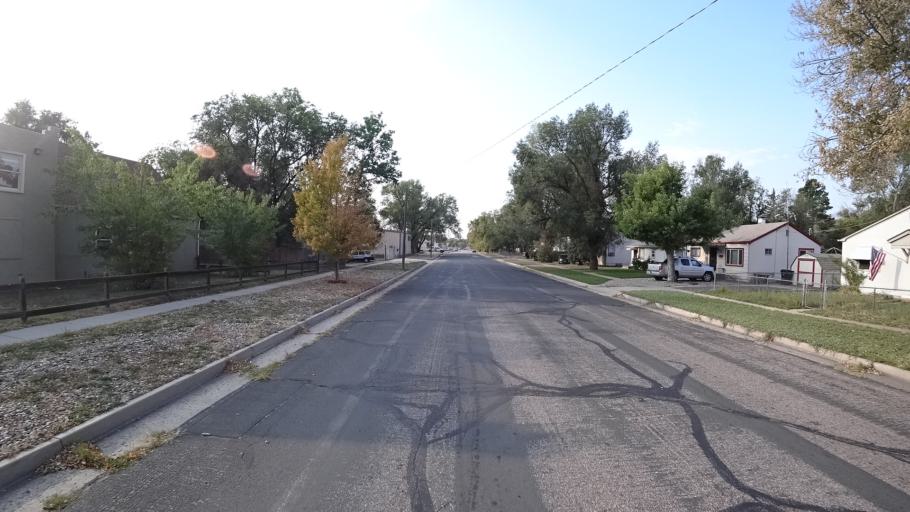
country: US
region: Colorado
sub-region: El Paso County
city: Colorado Springs
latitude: 38.8408
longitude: -104.7900
